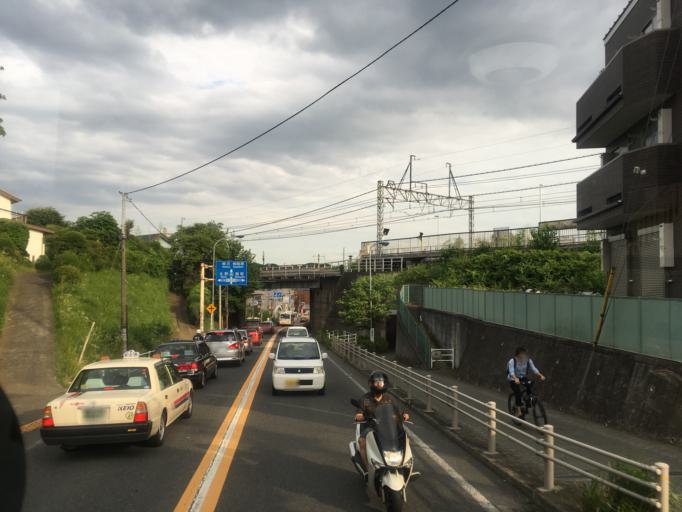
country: JP
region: Tokyo
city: Hachioji
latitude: 35.6446
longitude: 139.3377
